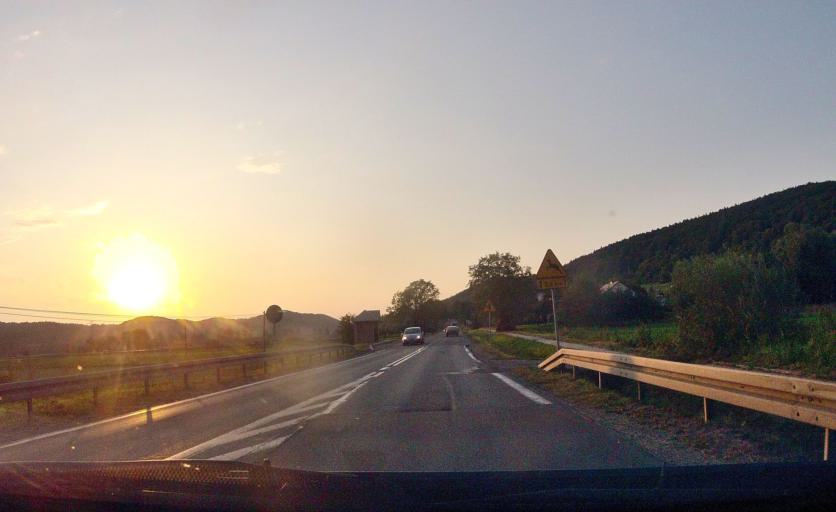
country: PL
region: Subcarpathian Voivodeship
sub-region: Powiat debicki
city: Brzostek
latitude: 49.8969
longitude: 21.3792
